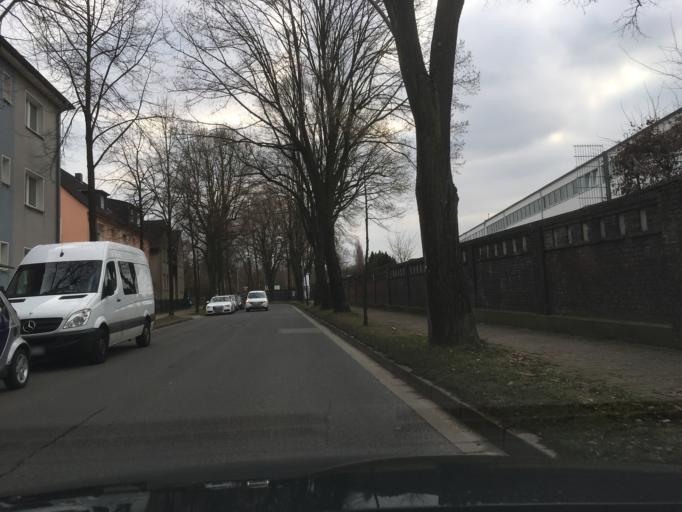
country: DE
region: North Rhine-Westphalia
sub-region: Regierungsbezirk Munster
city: Gladbeck
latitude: 51.5448
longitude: 7.0044
